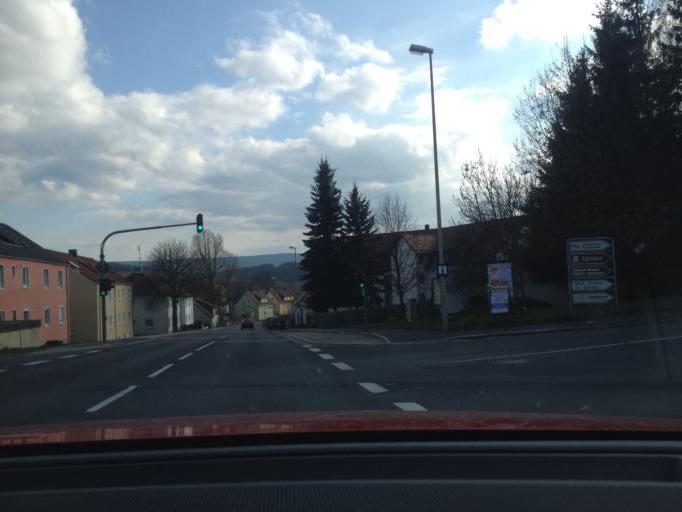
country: DE
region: Bavaria
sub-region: Upper Palatinate
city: Waldershof
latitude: 49.9815
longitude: 12.0681
